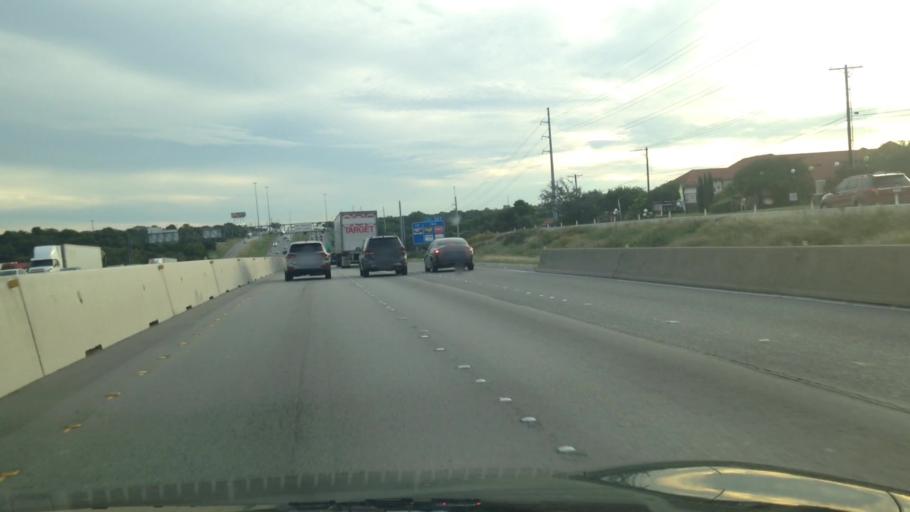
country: US
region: Texas
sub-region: Travis County
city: Onion Creek
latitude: 30.1832
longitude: -97.7756
